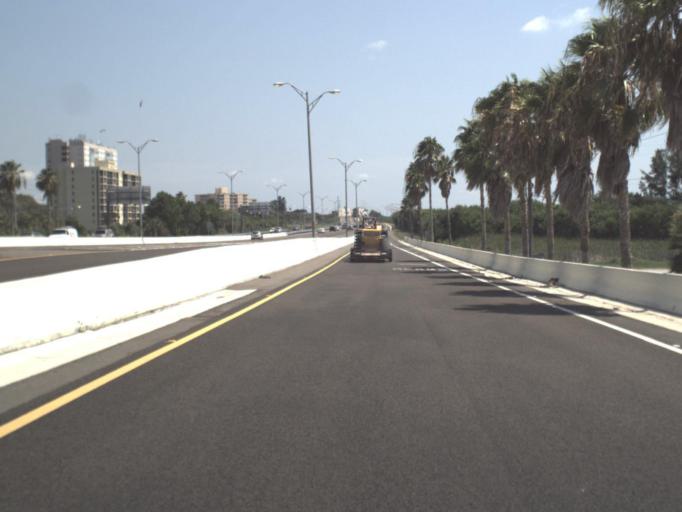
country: US
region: Florida
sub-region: Pinellas County
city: Tierra Verde
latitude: 27.7073
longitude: -82.6795
